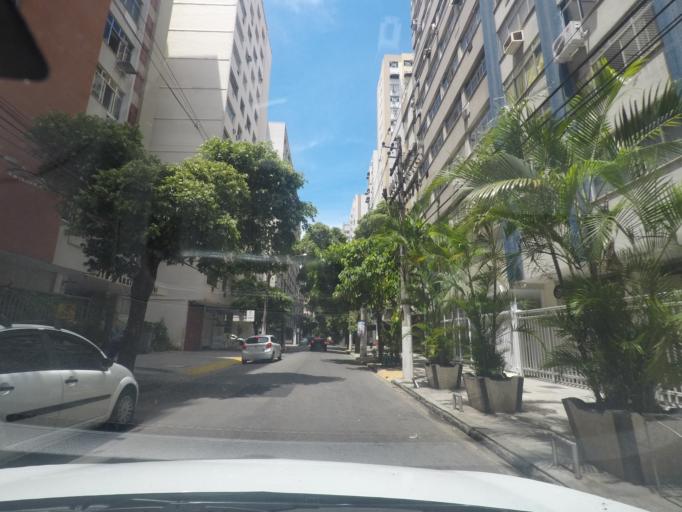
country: BR
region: Rio de Janeiro
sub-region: Niteroi
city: Niteroi
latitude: -22.9066
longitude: -43.1120
